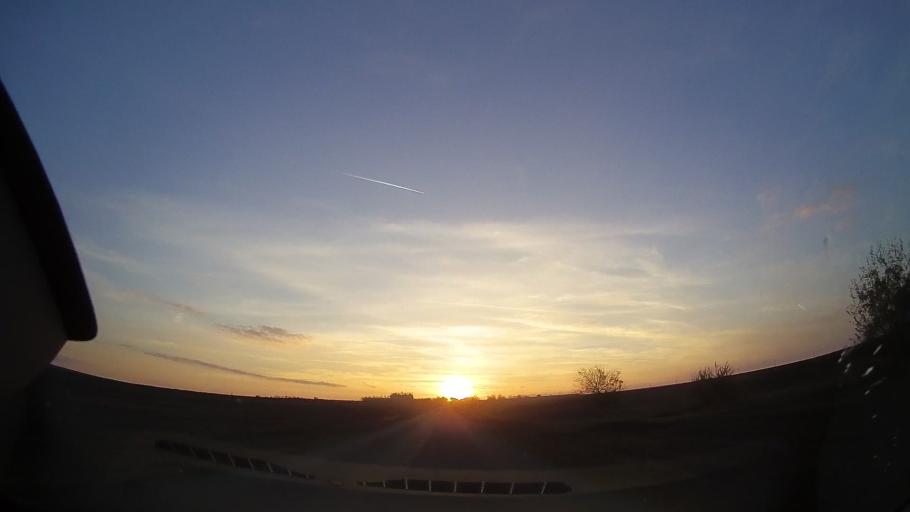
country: RO
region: Constanta
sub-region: Comuna Mereni
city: Mereni
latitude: 44.0245
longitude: 28.3609
